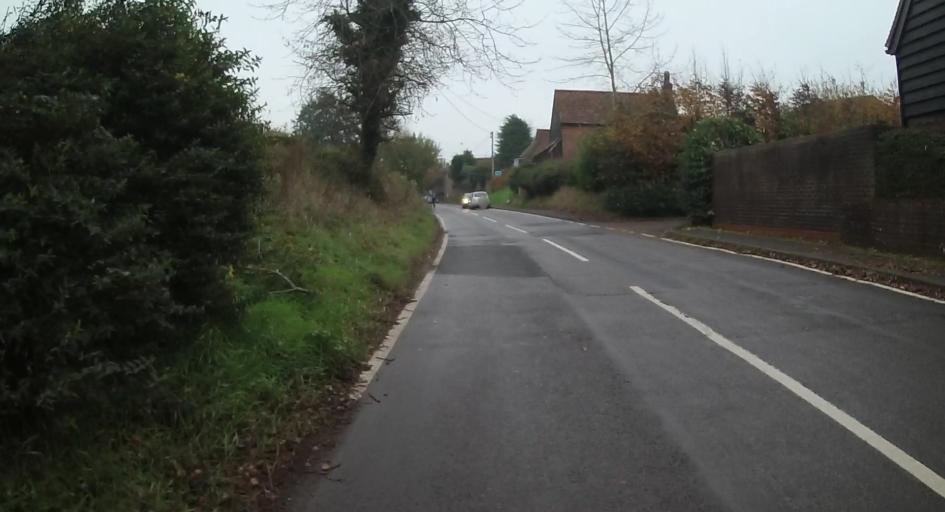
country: GB
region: England
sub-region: Hampshire
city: Kingsley
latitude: 51.1640
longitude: -0.8982
